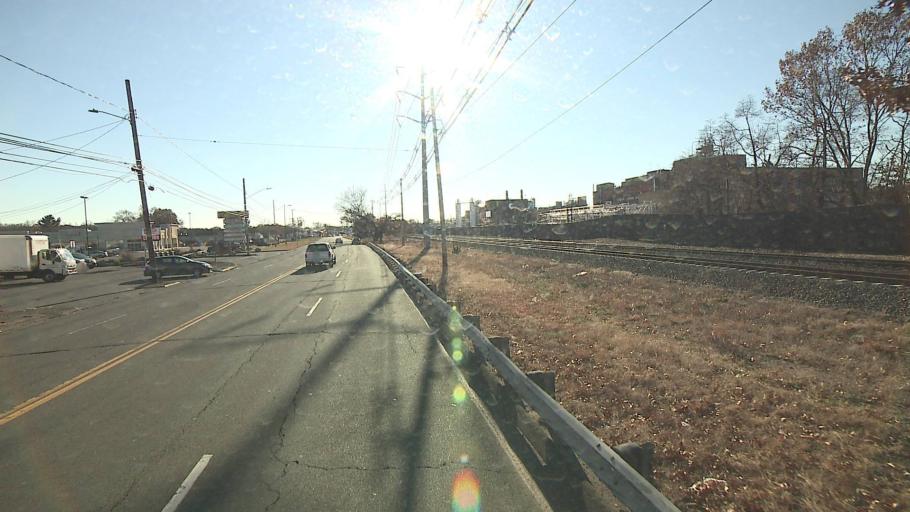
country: US
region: Connecticut
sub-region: New Haven County
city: Wallingford Center
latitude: 41.4367
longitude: -72.8337
